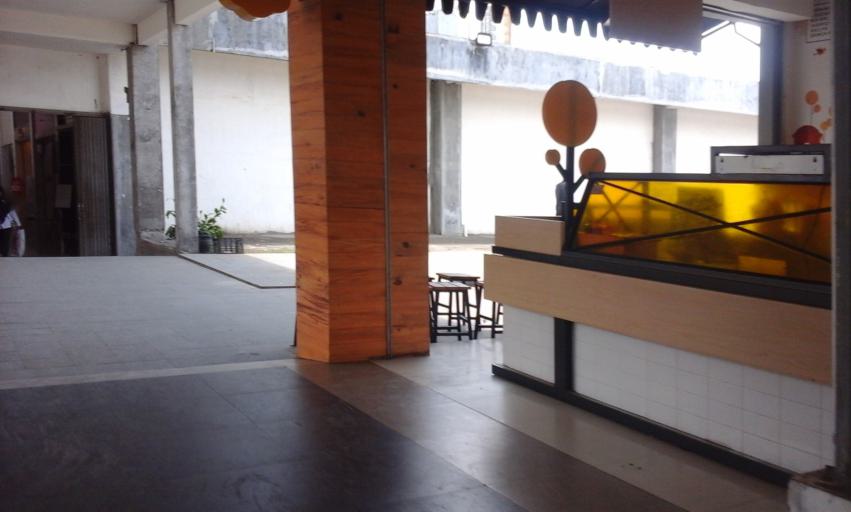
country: ID
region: East Java
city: Krajan
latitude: -8.1827
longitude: 113.6631
